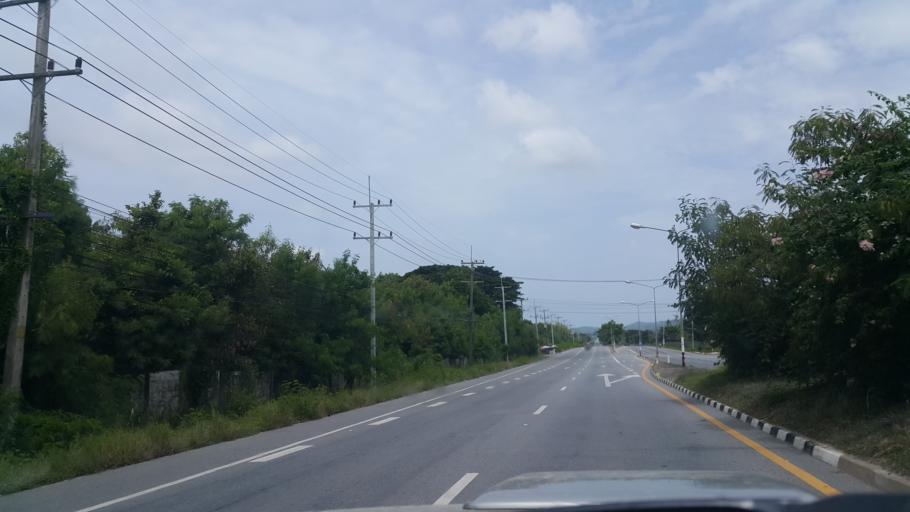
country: TH
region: Rayong
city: Ban Chang
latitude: 12.7071
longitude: 101.0213
